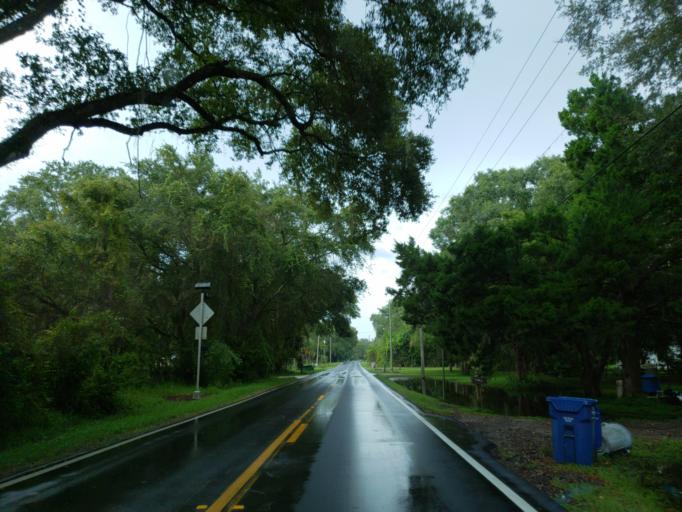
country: US
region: Florida
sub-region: Pasco County
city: Land O' Lakes
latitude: 28.2800
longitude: -82.4359
